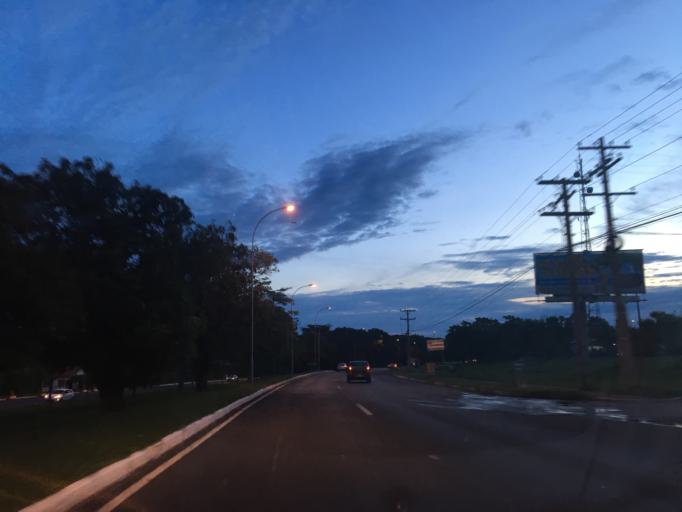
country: BR
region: Federal District
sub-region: Brasilia
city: Brasilia
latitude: -15.8370
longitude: -47.8668
